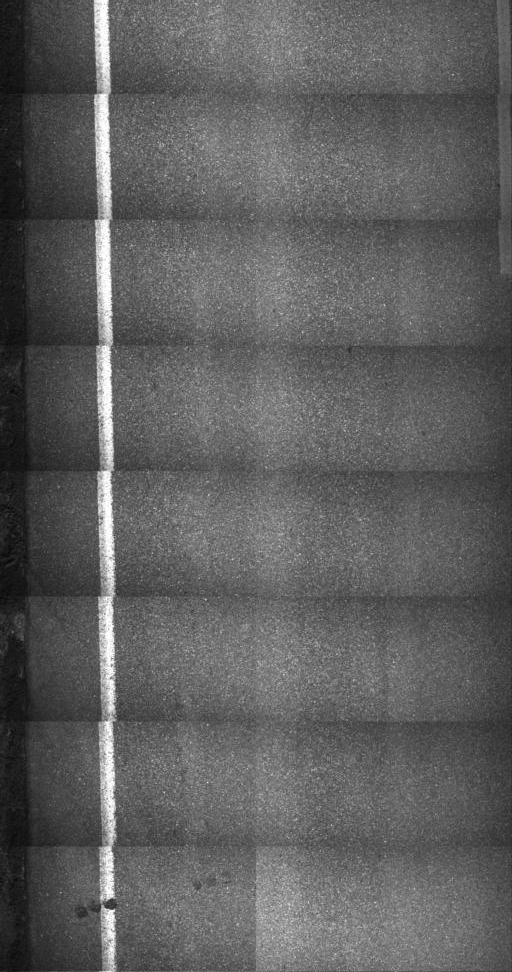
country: US
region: New York
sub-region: Essex County
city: Port Henry
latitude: 44.0800
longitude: -73.3760
